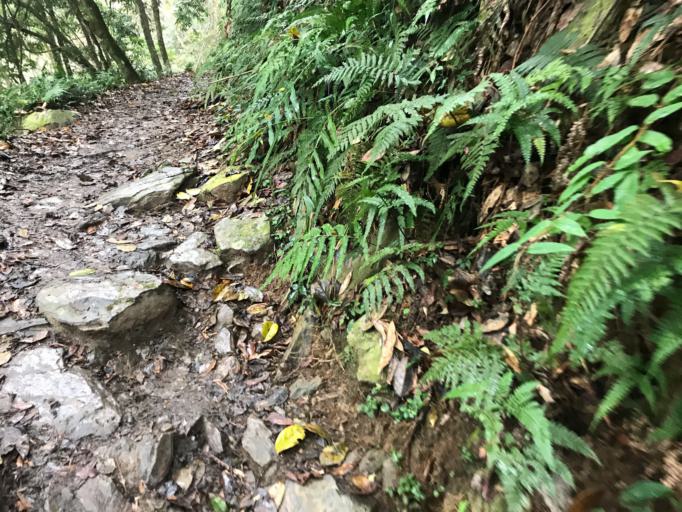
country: TW
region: Taiwan
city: Daxi
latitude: 24.5522
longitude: 121.2919
